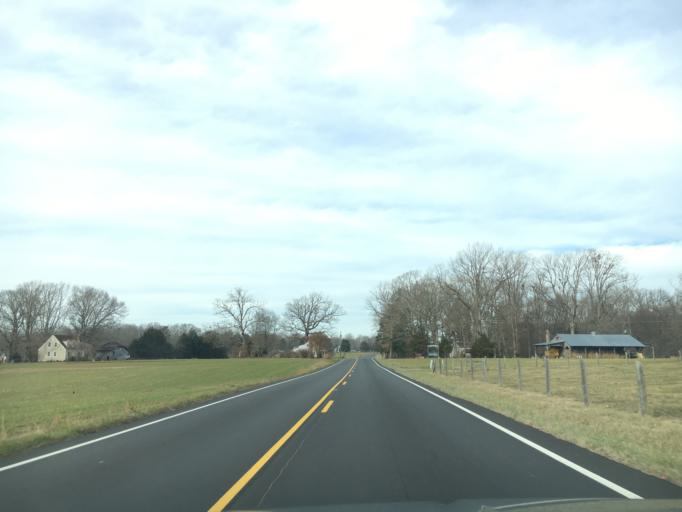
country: US
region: Virginia
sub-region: Goochland County
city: Goochland
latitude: 37.8095
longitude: -77.8657
